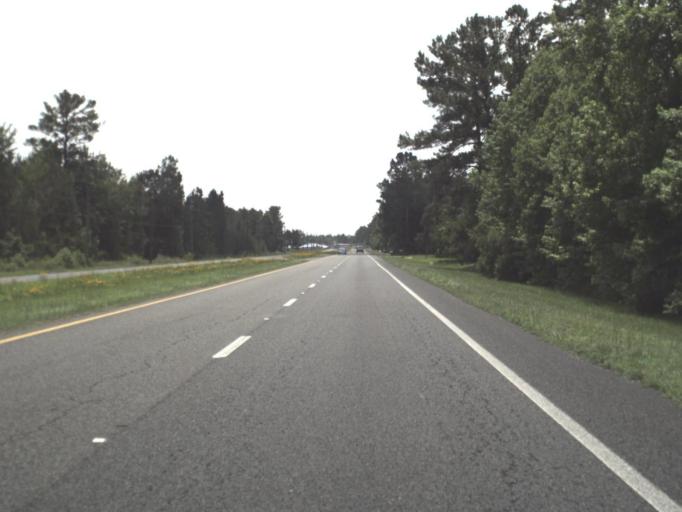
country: US
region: Florida
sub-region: Nassau County
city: Callahan
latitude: 30.5991
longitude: -81.8333
